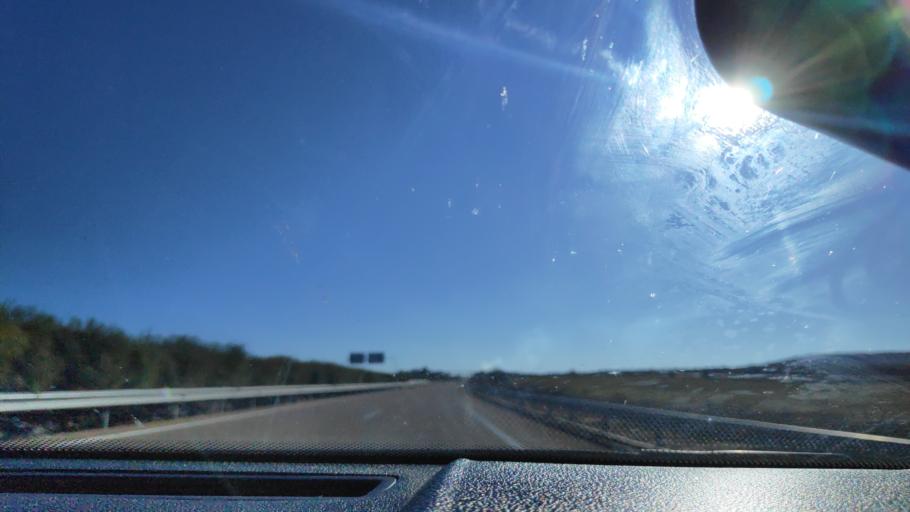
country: ES
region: Extremadura
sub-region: Provincia de Badajoz
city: Villafranca de los Barros
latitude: 38.5225
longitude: -6.3499
